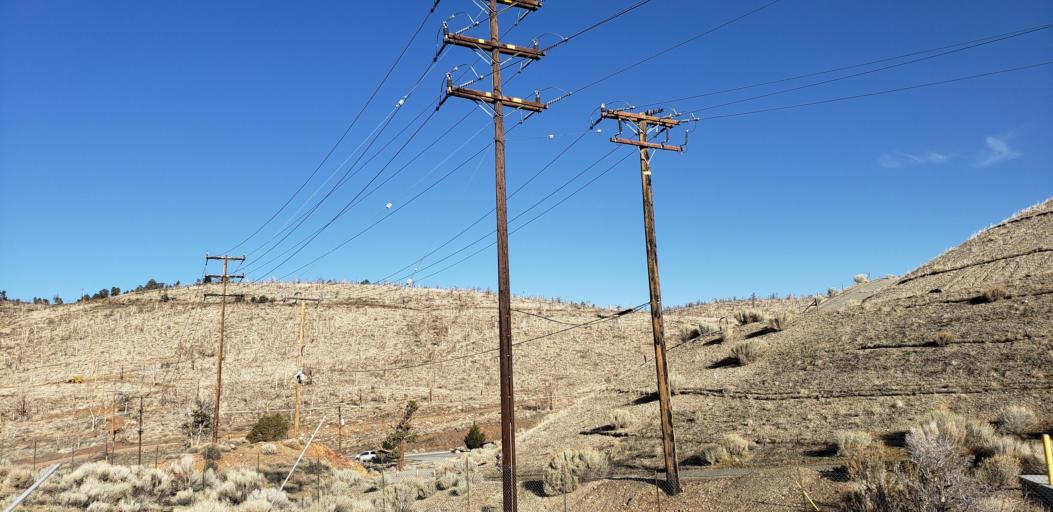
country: US
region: California
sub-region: San Bernardino County
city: Big Bear City
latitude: 34.3039
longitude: -116.8208
